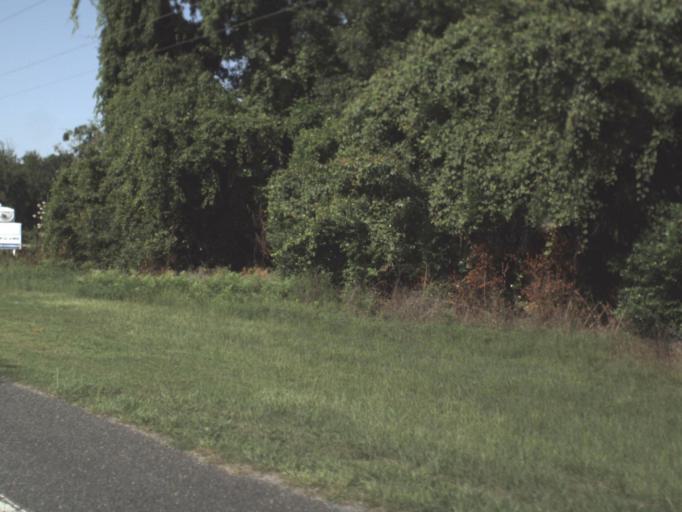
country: US
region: Florida
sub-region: Alachua County
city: High Springs
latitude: 29.9330
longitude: -82.7138
